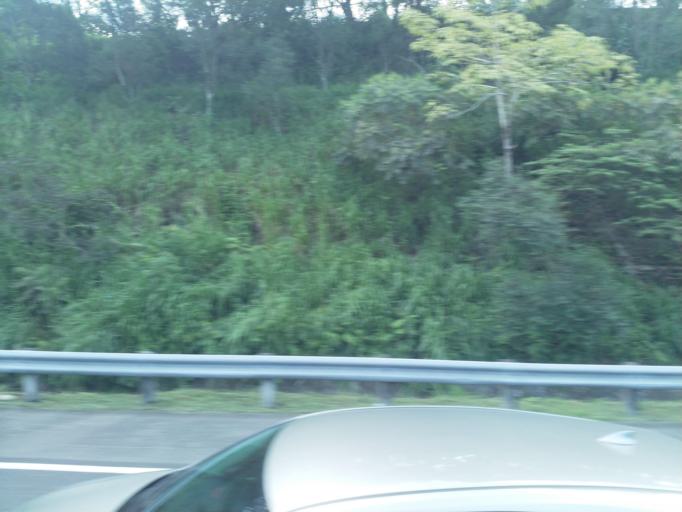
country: TW
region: Taiwan
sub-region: Pingtung
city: Pingtung
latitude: 22.7780
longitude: 120.4213
